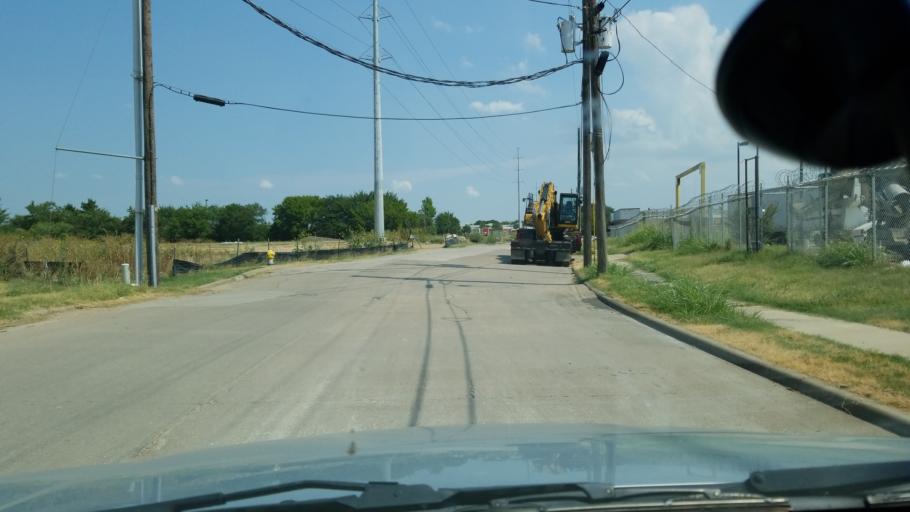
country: US
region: Texas
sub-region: Dallas County
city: Farmers Branch
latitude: 32.8691
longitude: -96.9053
